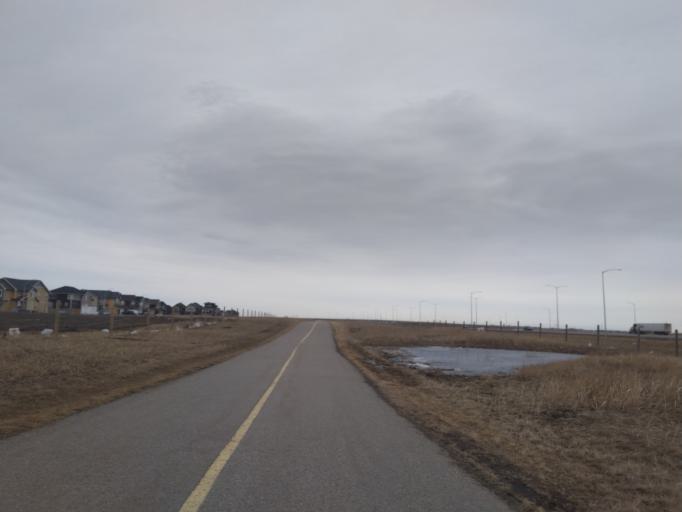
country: CA
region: Alberta
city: Chestermere
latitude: 51.1278
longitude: -113.9227
